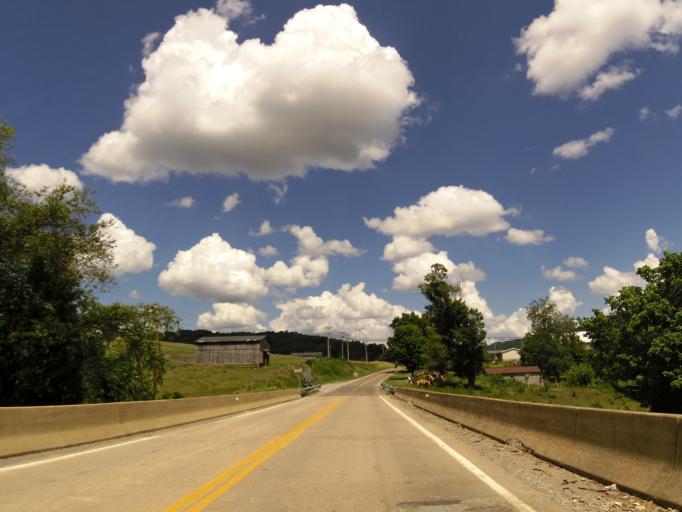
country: US
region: Virginia
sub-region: Lee County
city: Pennington Gap
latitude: 36.6980
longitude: -83.0178
